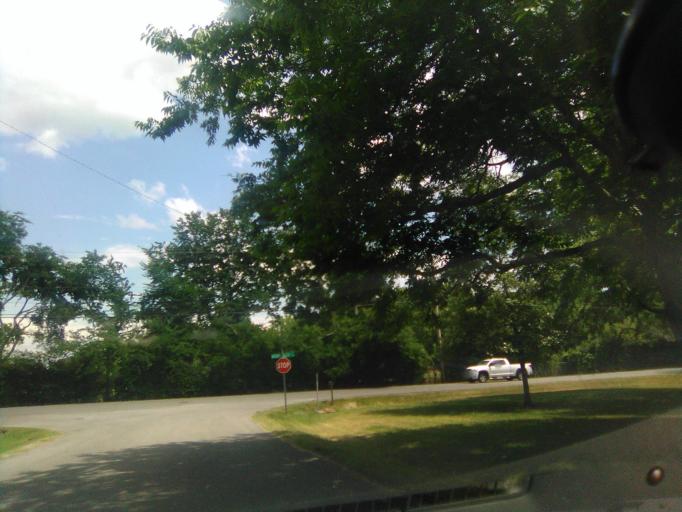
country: US
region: Tennessee
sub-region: Davidson County
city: Belle Meade
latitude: 36.1217
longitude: -86.8732
